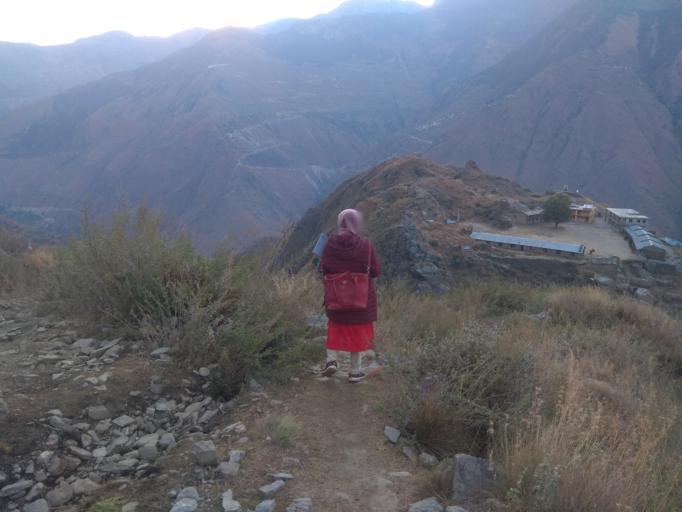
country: NP
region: Mid Western
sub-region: Bheri Zone
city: Dailekh
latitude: 29.2846
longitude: 81.7186
